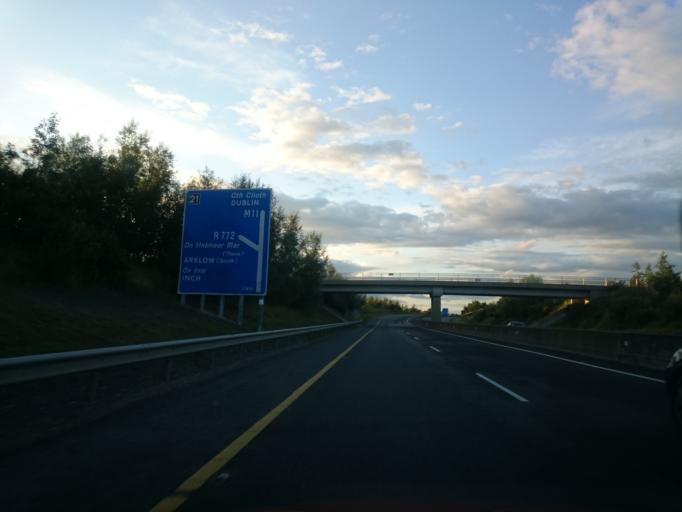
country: IE
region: Leinster
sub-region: Loch Garman
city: Castletown
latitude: 52.7615
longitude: -6.1940
